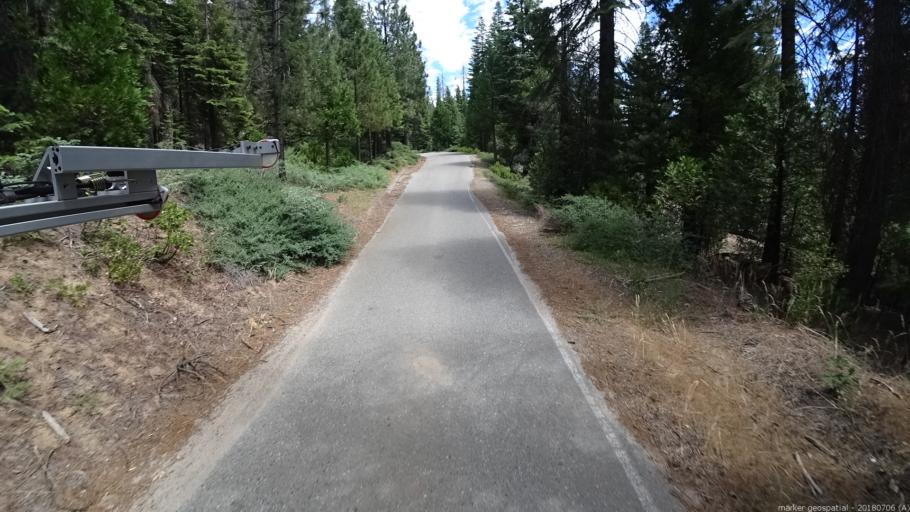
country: US
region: California
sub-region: Madera County
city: Oakhurst
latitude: 37.4208
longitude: -119.4134
